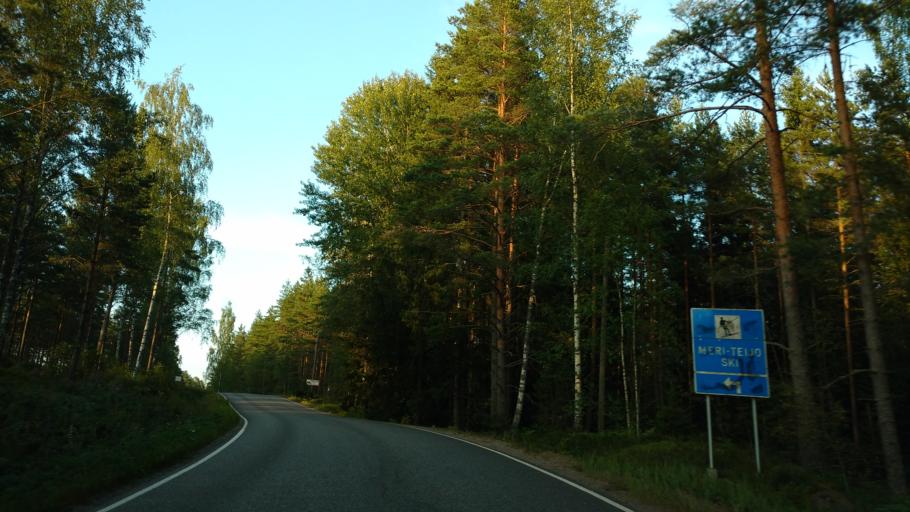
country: FI
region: Varsinais-Suomi
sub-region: Salo
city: Saerkisalo
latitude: 60.2304
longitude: 22.9359
